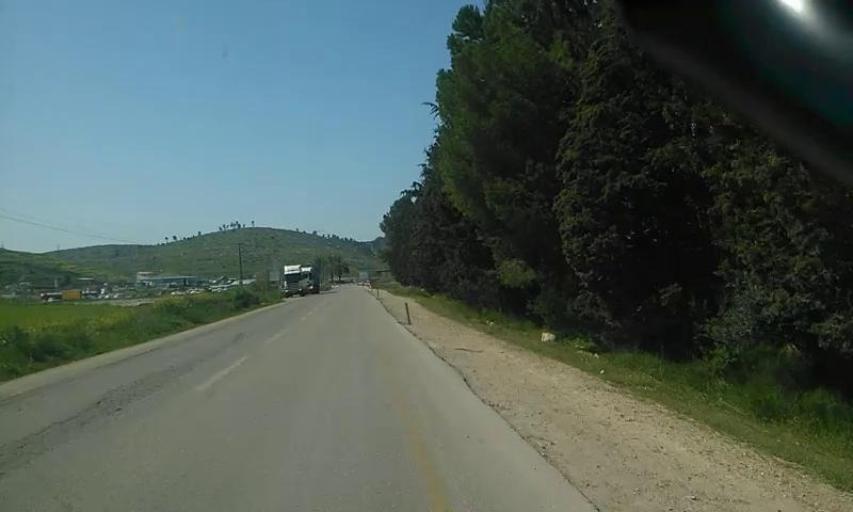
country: PS
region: West Bank
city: Idhna
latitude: 31.5901
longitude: 34.9665
